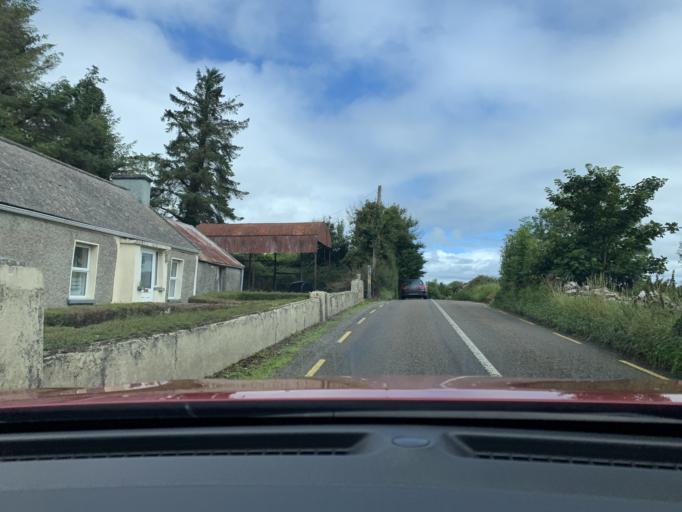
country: IE
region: Connaught
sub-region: County Leitrim
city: Carrick-on-Shannon
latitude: 53.9177
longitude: -8.1233
